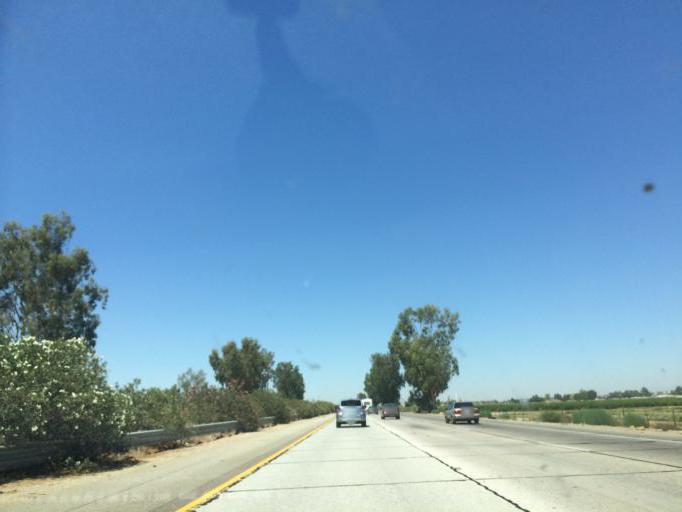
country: US
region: California
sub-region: Kern County
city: Greenfield
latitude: 35.2128
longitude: -119.0109
